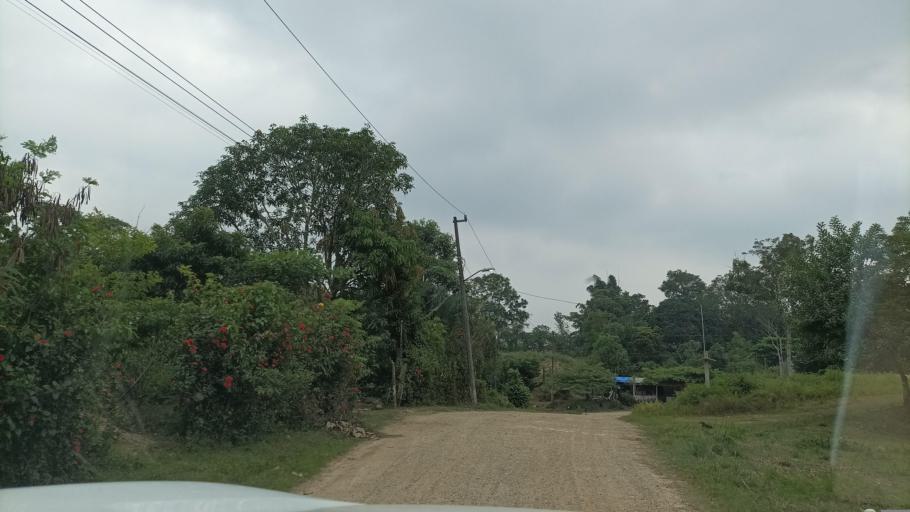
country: MX
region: Veracruz
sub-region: Moloacan
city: Cuichapa
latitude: 17.5800
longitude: -94.2270
